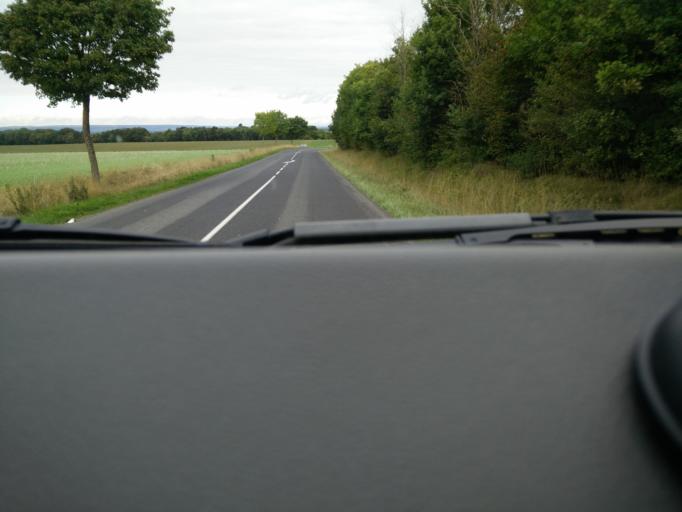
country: FR
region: Lorraine
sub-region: Departement de Meurthe-et-Moselle
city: Montauville
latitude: 48.9330
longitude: 5.8956
